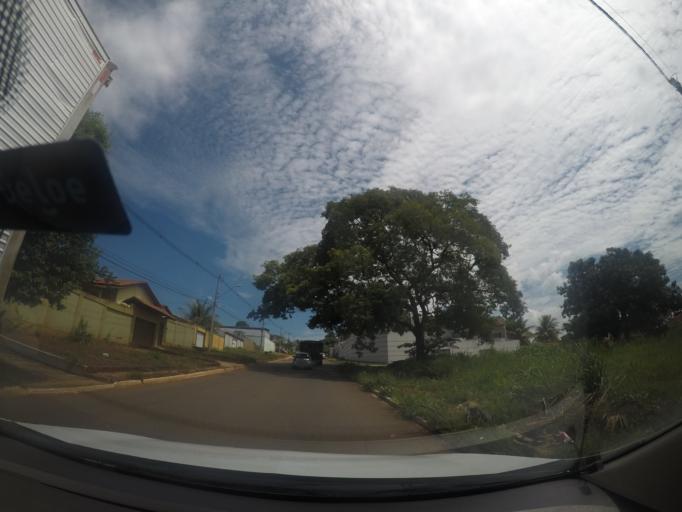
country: BR
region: Goias
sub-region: Goiania
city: Goiania
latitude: -16.6637
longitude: -49.3333
